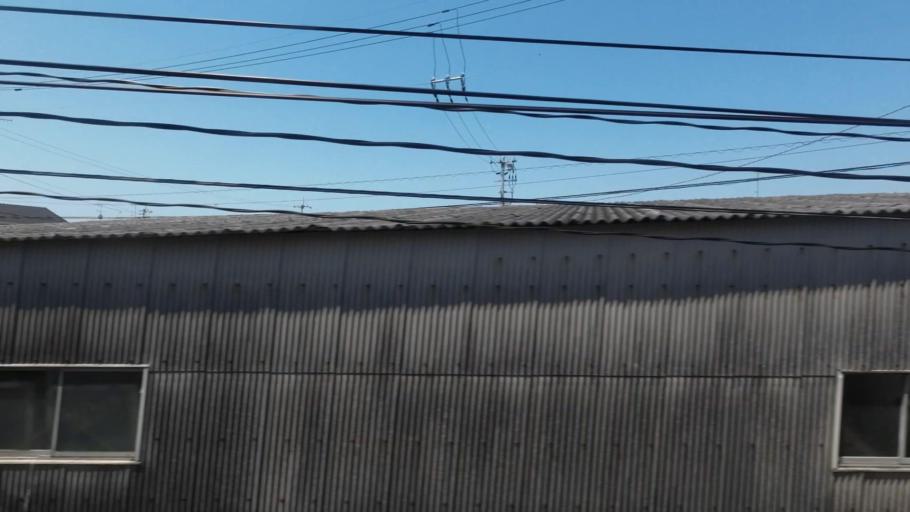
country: JP
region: Ehime
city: Hojo
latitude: 33.9593
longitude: 132.7750
